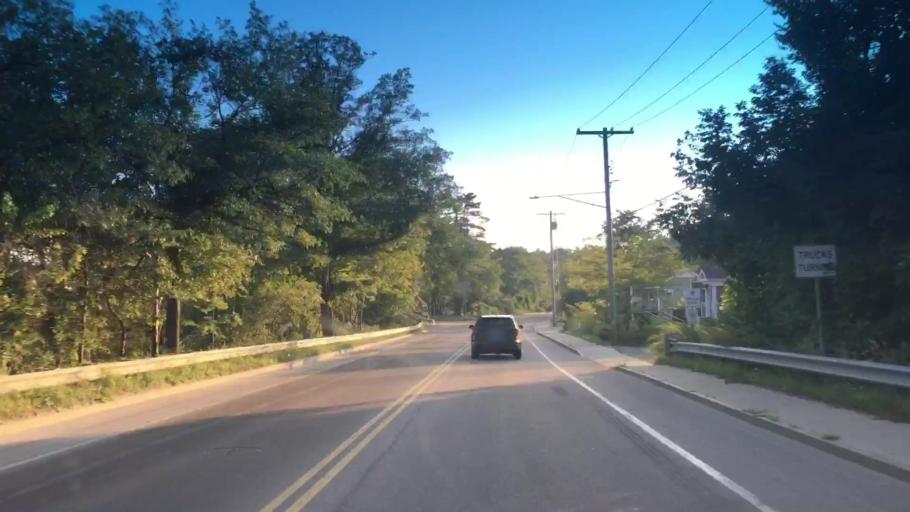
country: US
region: Massachusetts
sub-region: Norfolk County
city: Medfield
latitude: 42.1836
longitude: -71.3144
